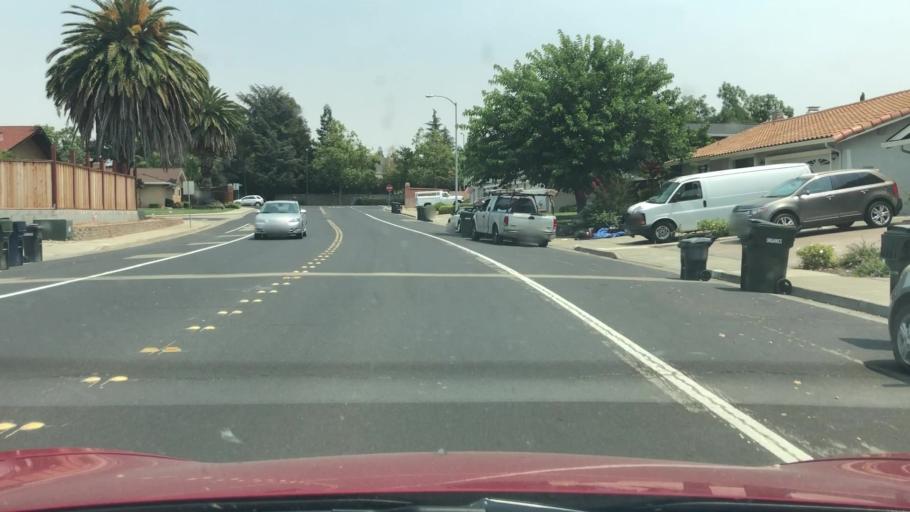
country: US
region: California
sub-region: Alameda County
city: Livermore
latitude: 37.6657
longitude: -121.7695
